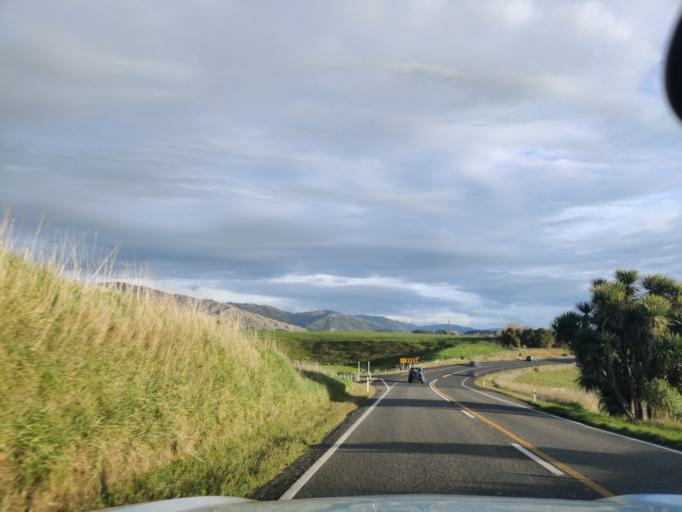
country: NZ
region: Manawatu-Wanganui
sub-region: Horowhenua District
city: Foxton
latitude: -40.5070
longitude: 175.4853
